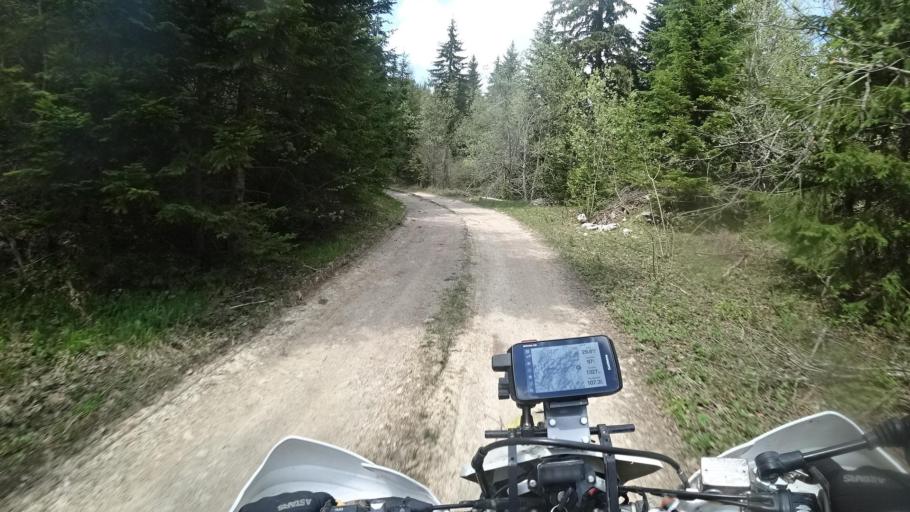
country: BA
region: Republika Srpska
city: Sipovo
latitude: 44.1201
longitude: 17.0798
